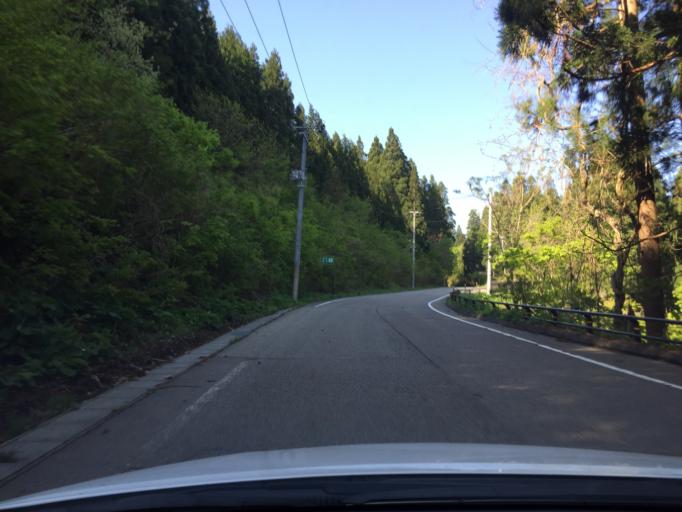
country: JP
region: Fukushima
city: Kitakata
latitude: 37.6884
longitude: 139.7028
